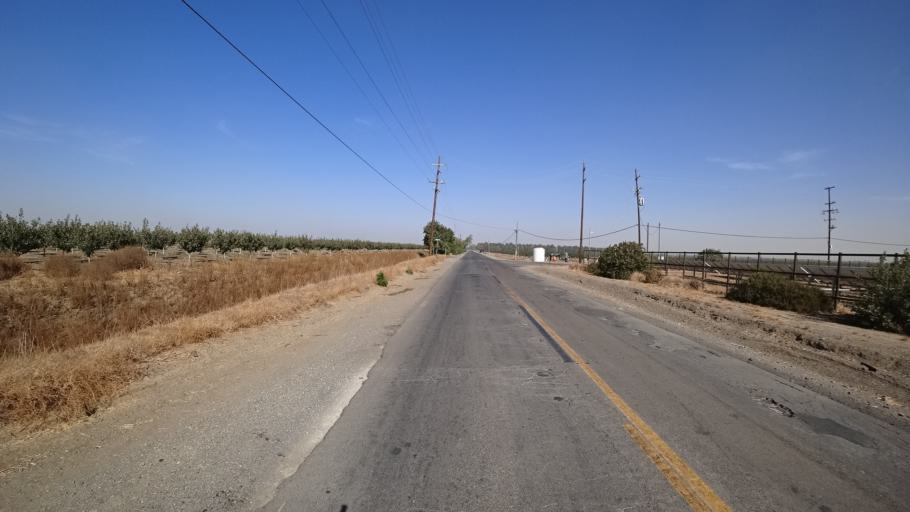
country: US
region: California
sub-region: Yolo County
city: Davis
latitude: 38.5015
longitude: -121.6956
